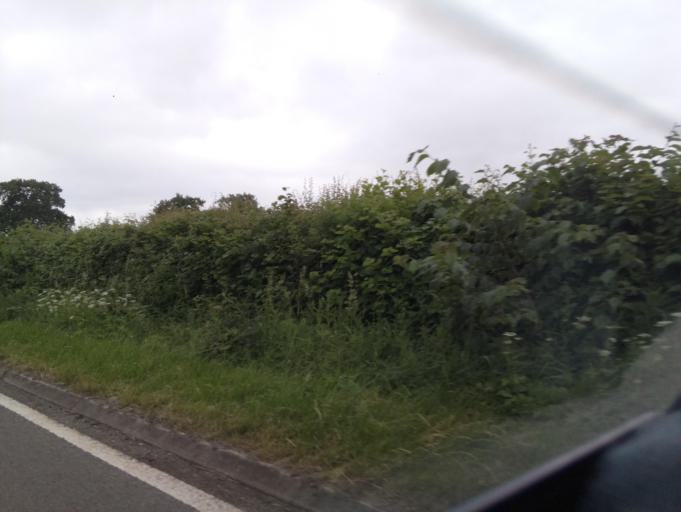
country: GB
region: England
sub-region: Derbyshire
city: Yeldersley
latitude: 52.9597
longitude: -1.5959
